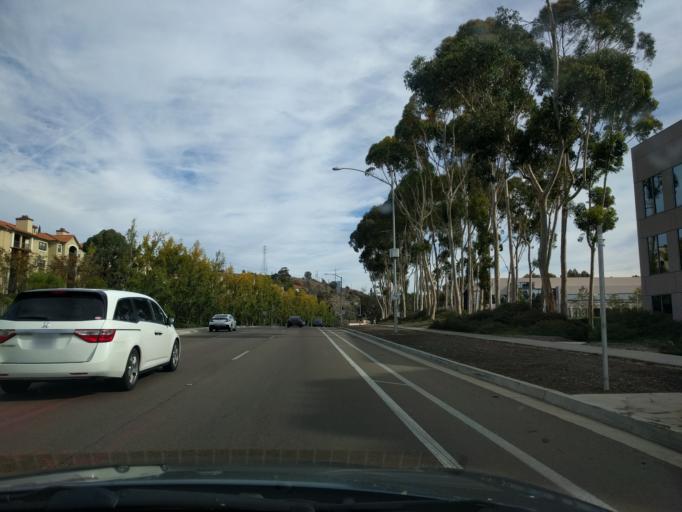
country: US
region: California
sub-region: San Diego County
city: San Diego
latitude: 32.7842
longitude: -117.1275
